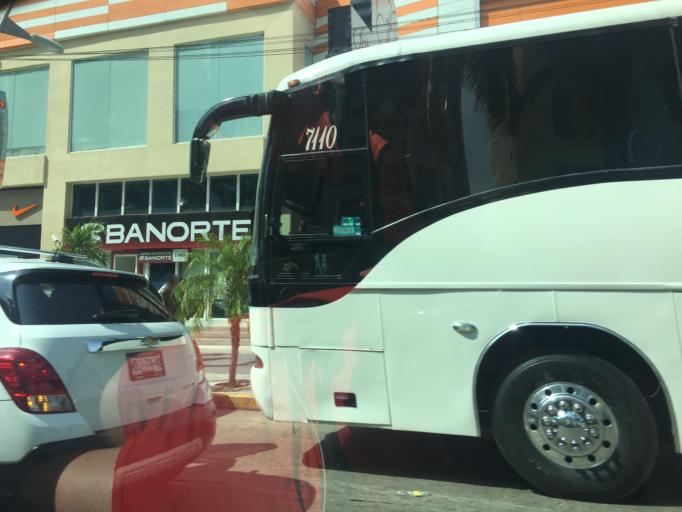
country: MX
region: Guerrero
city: Acapulco de Juarez
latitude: 16.8610
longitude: -99.8813
